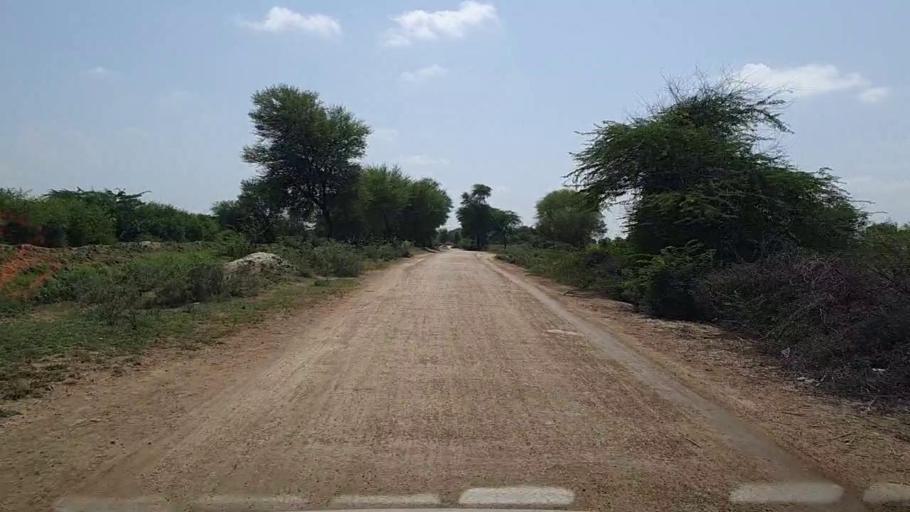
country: PK
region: Sindh
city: Kario
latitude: 24.8672
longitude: 68.6874
